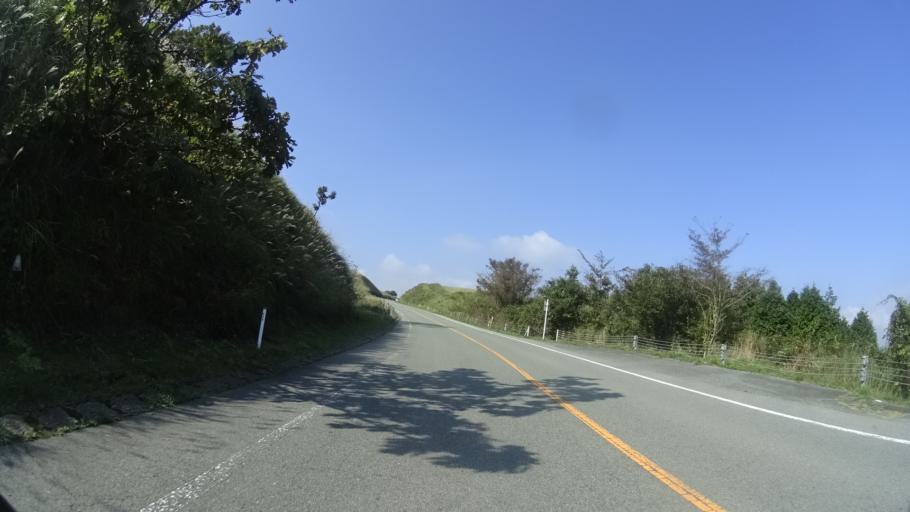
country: JP
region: Kumamoto
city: Aso
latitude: 33.0159
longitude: 131.0689
